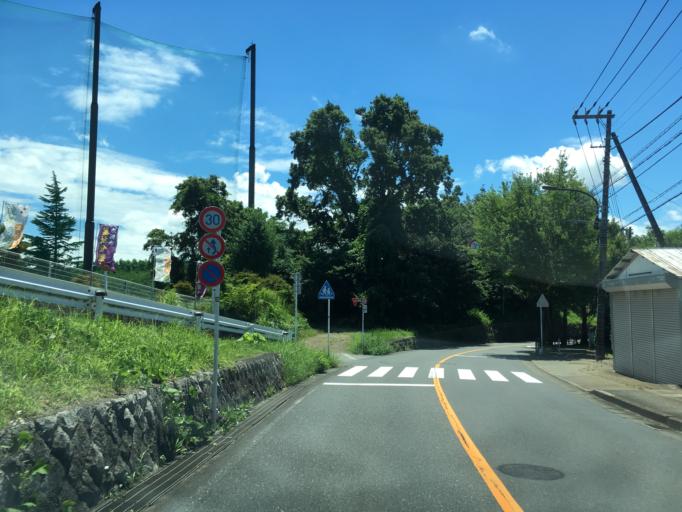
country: JP
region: Tokyo
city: Kokubunji
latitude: 35.6373
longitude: 139.4647
